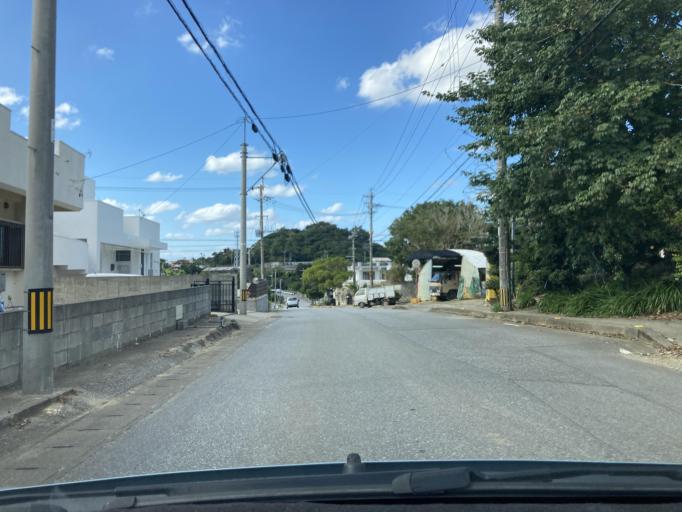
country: JP
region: Okinawa
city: Gushikawa
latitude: 26.3714
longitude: 127.8376
